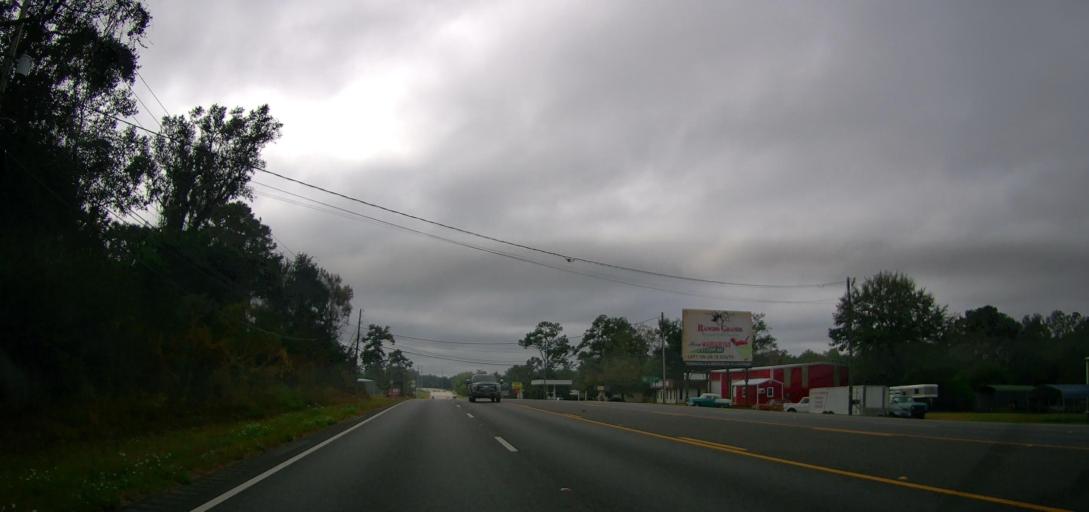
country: US
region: Georgia
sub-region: Thomas County
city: Thomasville
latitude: 30.8770
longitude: -83.9346
